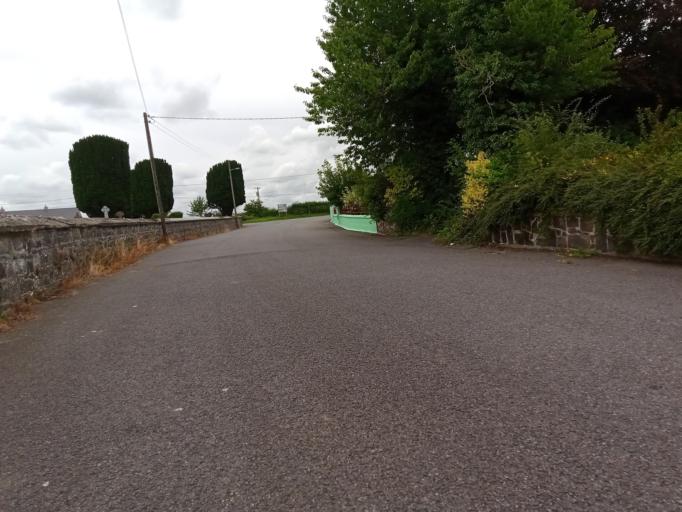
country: IE
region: Leinster
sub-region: Kilkenny
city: Callan
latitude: 52.5310
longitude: -7.4112
